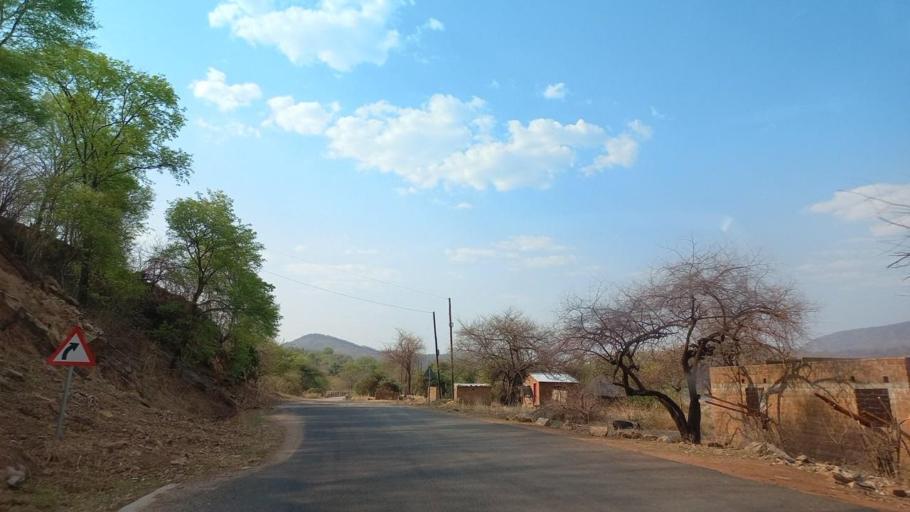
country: ZM
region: Lusaka
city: Luangwa
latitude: -14.9974
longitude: 30.2144
